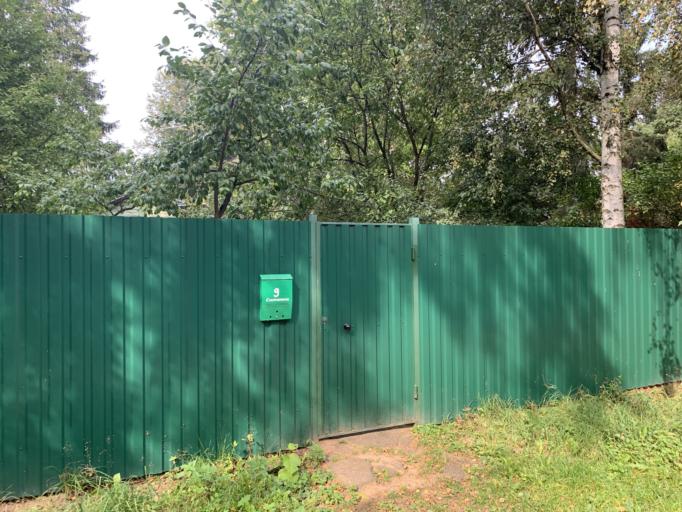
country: RU
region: Moskovskaya
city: Cherkizovo
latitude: 55.9538
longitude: 37.8028
